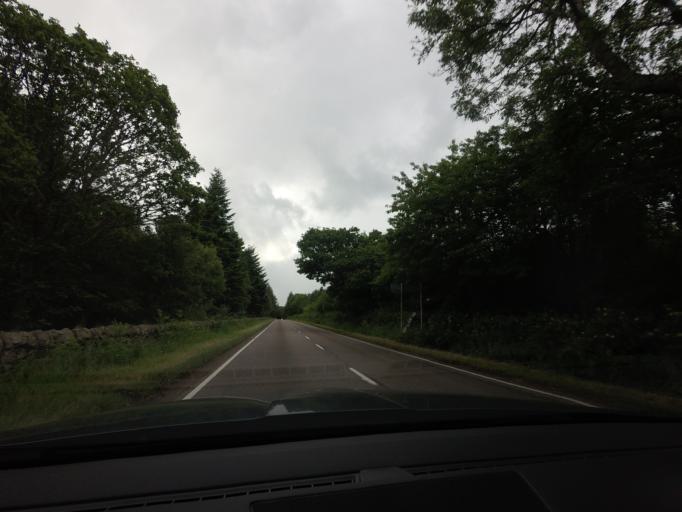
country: GB
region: Scotland
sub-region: Moray
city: Findochty
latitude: 57.6829
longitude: -2.8880
